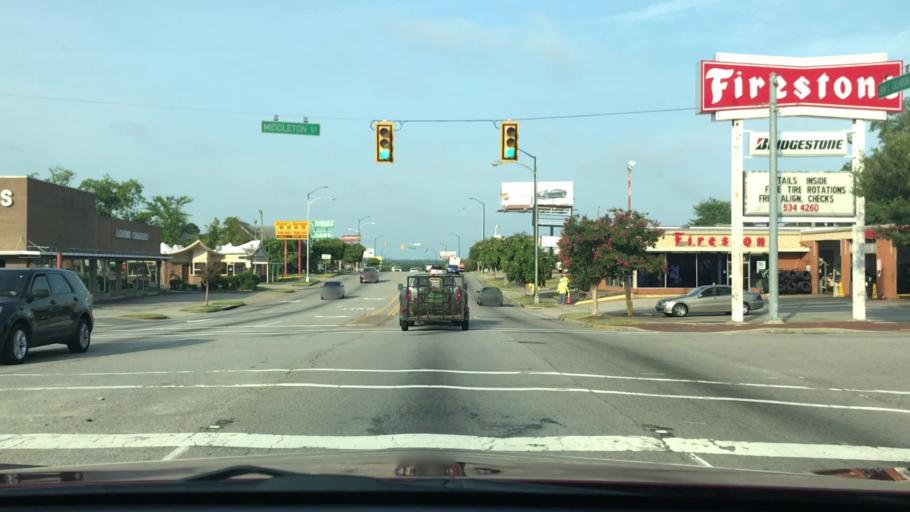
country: US
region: South Carolina
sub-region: Orangeburg County
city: Orangeburg
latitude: 33.4876
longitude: -80.8614
